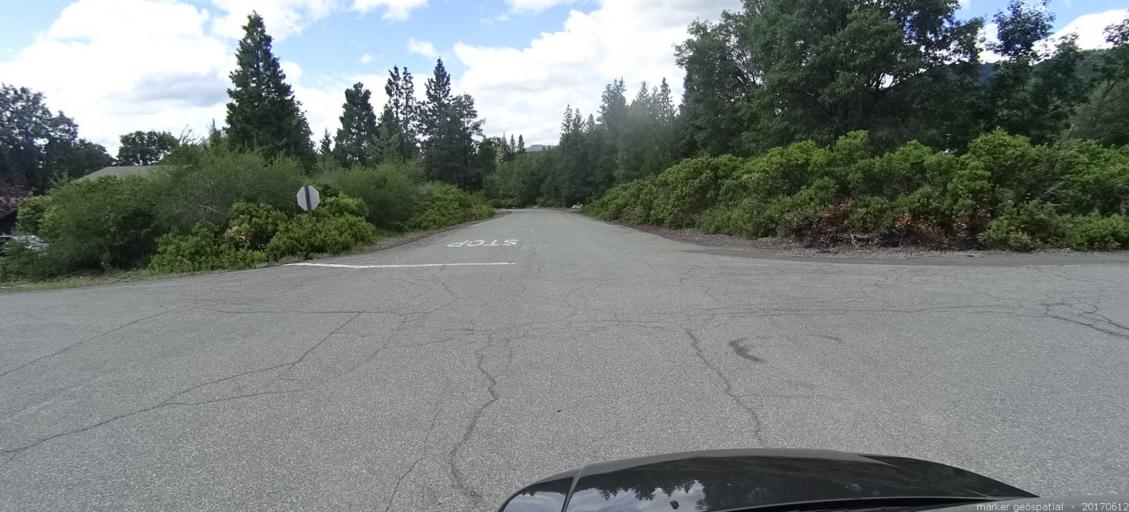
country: US
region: California
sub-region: Siskiyou County
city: Mount Shasta
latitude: 41.3156
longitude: -122.2840
